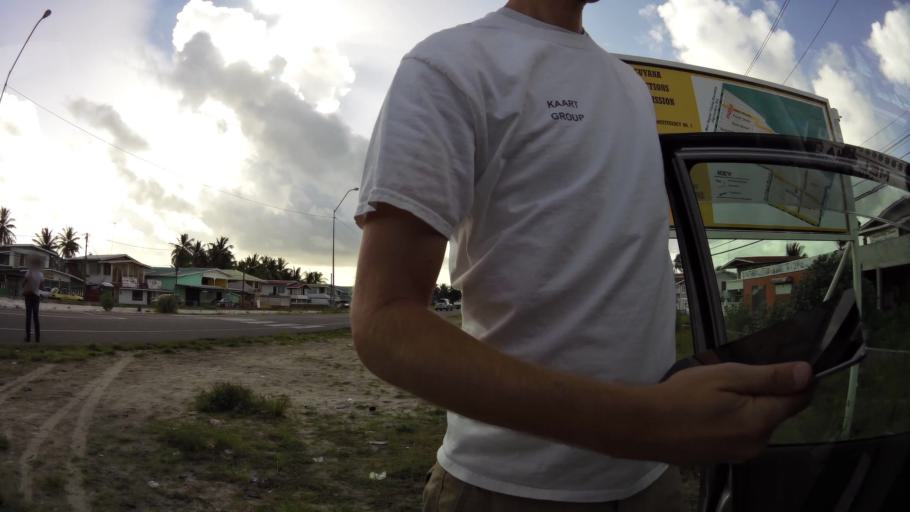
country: GY
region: Demerara-Mahaica
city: Georgetown
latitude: 6.8048
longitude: -58.0494
